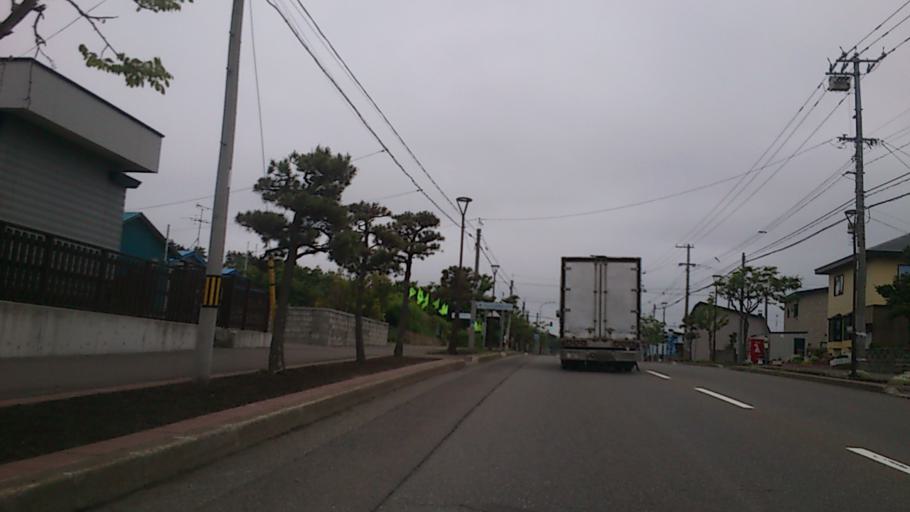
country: JP
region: Hokkaido
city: Iwanai
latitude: 42.4516
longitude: 139.8524
